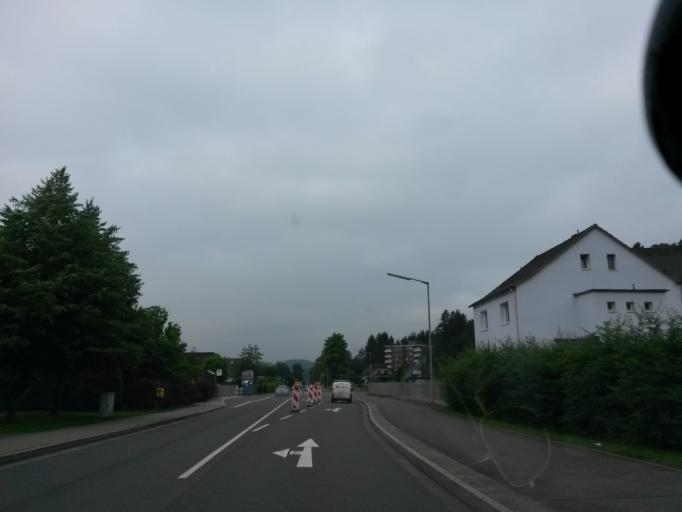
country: DE
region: North Rhine-Westphalia
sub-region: Regierungsbezirk Koln
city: Engelskirchen
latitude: 50.9866
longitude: 7.3886
